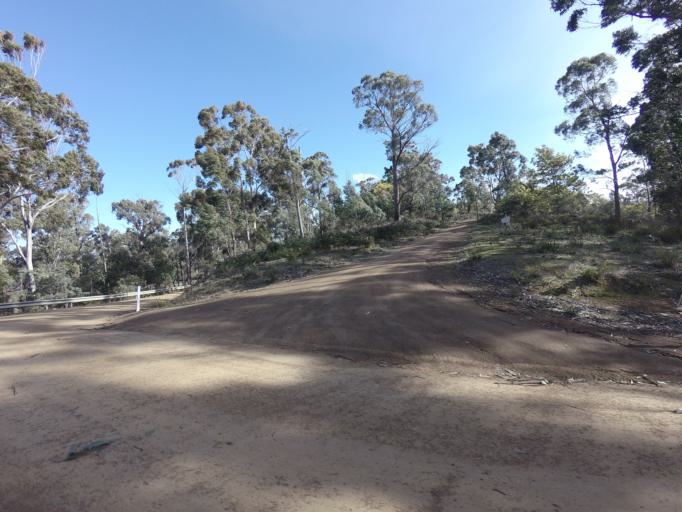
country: AU
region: Tasmania
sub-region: Kingborough
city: Kettering
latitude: -43.0911
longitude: 147.2669
